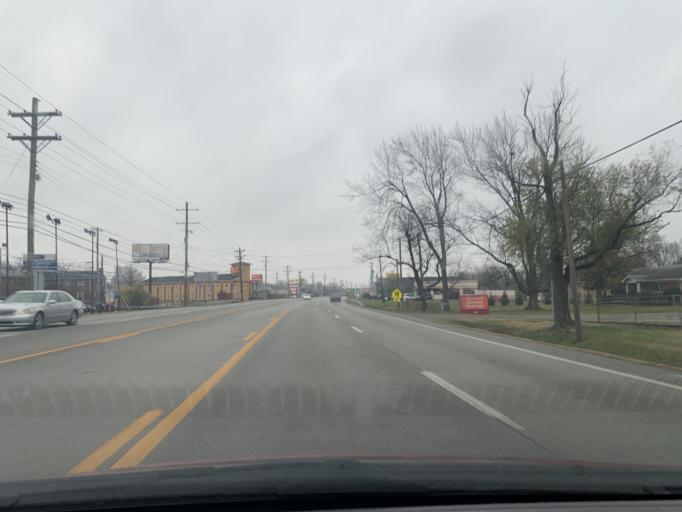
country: US
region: Kentucky
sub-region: Jefferson County
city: Okolona
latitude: 38.1636
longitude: -85.7012
